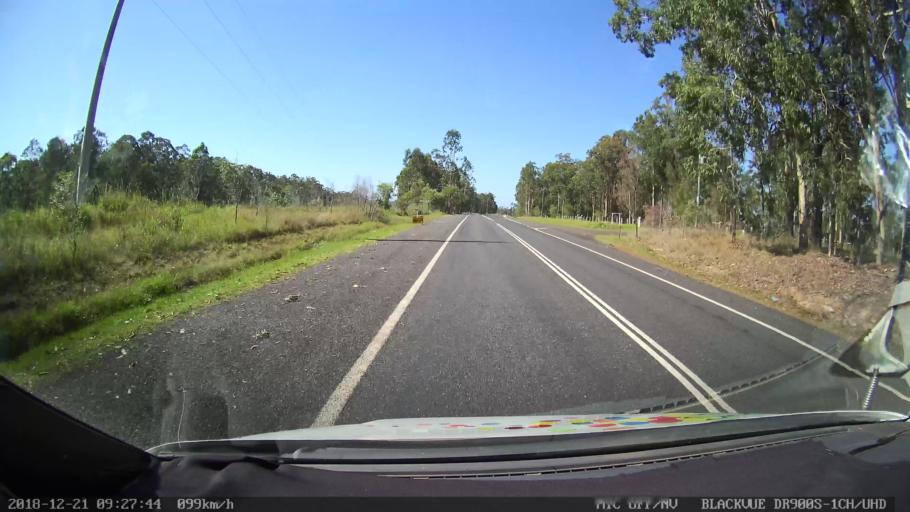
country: AU
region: New South Wales
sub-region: Clarence Valley
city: Maclean
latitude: -29.4071
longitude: 152.9888
